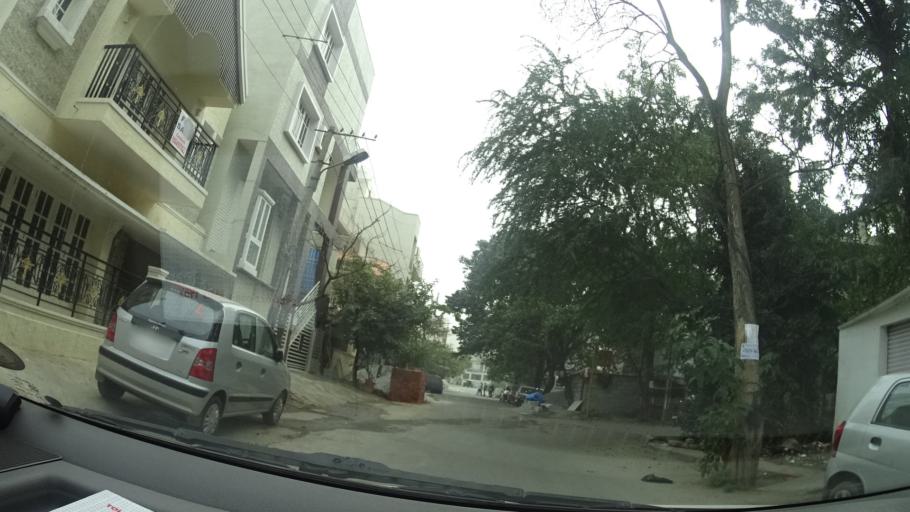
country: IN
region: Karnataka
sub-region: Bangalore Urban
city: Bangalore
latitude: 13.0310
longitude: 77.6291
